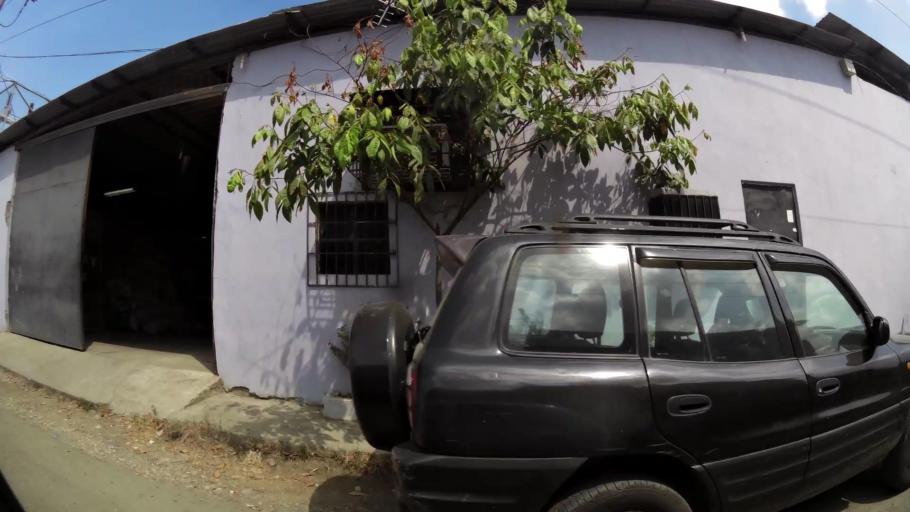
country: EC
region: Guayas
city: Guayaquil
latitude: -2.1367
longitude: -79.9383
